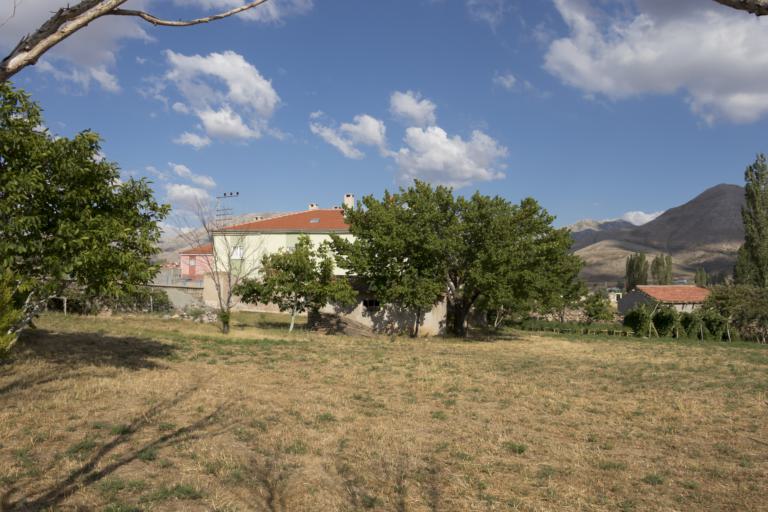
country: TR
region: Kayseri
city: Toklar
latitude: 38.4084
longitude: 36.0748
